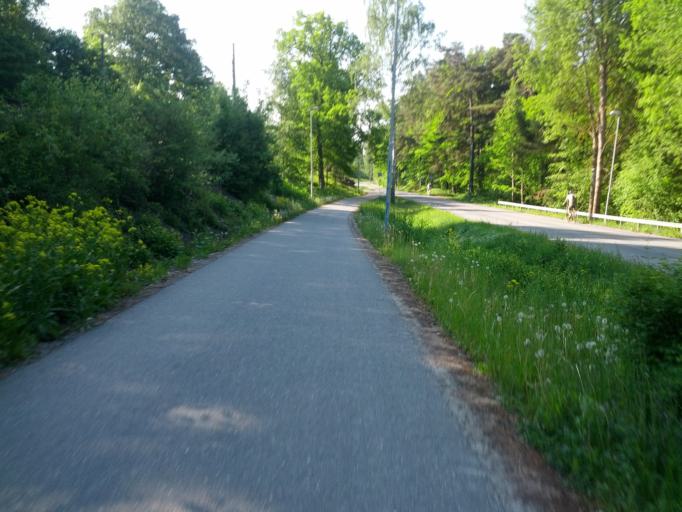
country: SE
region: Stockholm
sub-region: Danderyds Kommun
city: Djursholm
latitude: 59.4090
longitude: 18.0594
